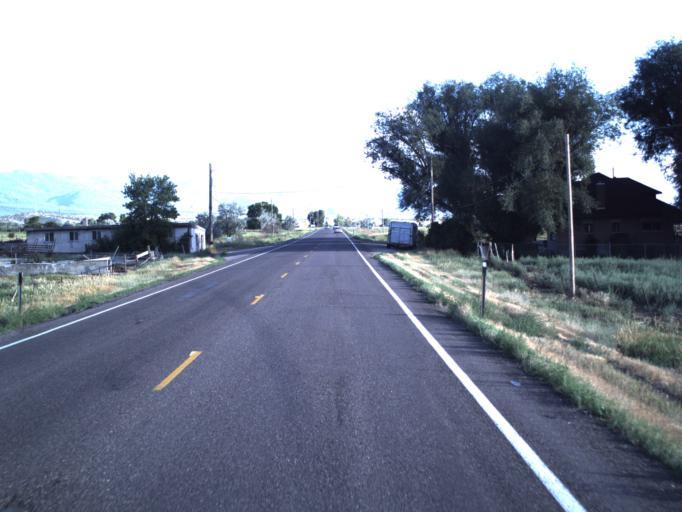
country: US
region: Utah
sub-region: Sanpete County
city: Fairview
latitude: 39.6024
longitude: -111.4448
